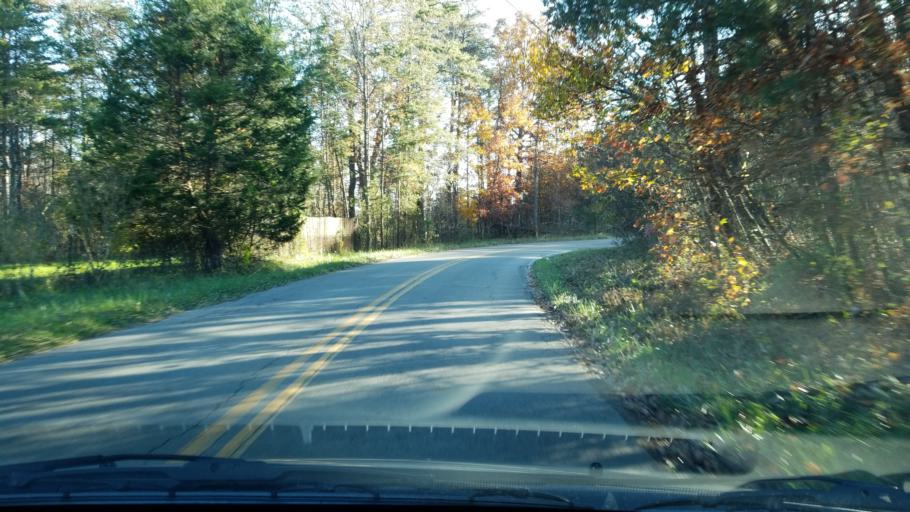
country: US
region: Tennessee
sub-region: Hamilton County
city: Falling Water
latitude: 35.2269
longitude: -85.2803
